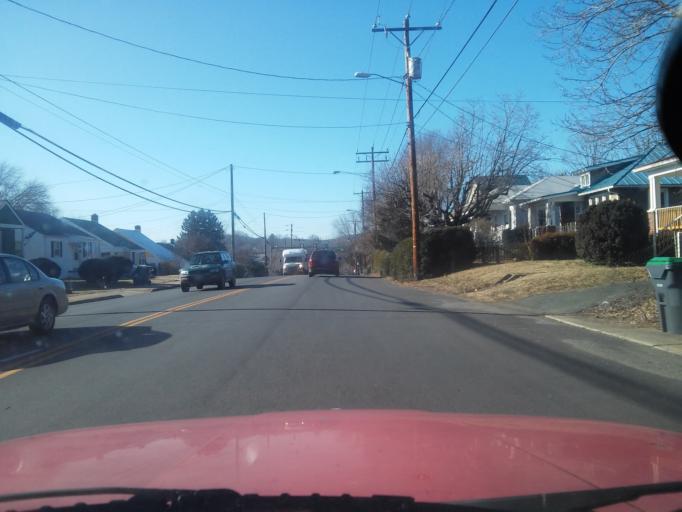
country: US
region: Virginia
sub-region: City of Charlottesville
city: Charlottesville
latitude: 38.0215
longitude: -78.4818
